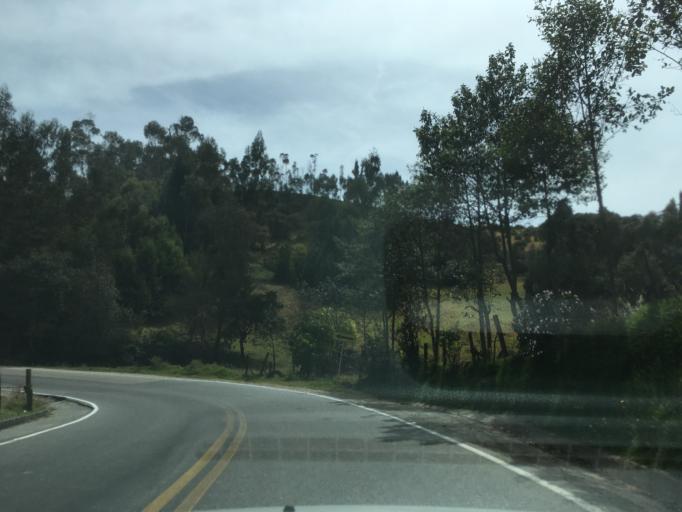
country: CO
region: Boyaca
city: Firavitoba
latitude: 5.6225
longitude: -72.9156
